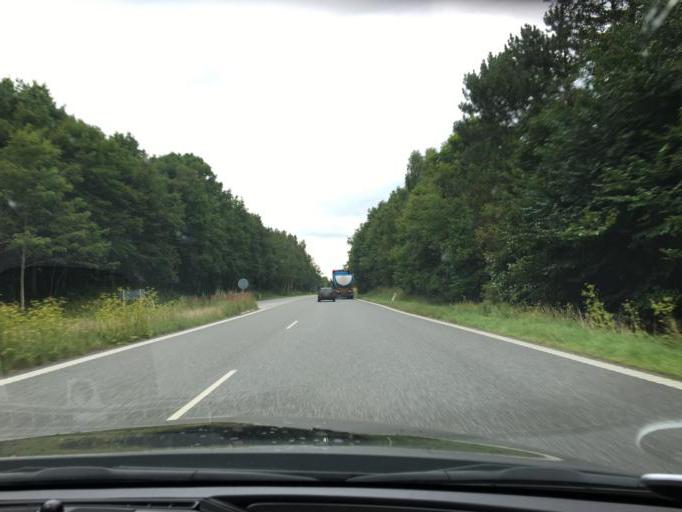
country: DK
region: Capital Region
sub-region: Hillerod Kommune
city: Nodebo
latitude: 55.9372
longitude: 12.3576
